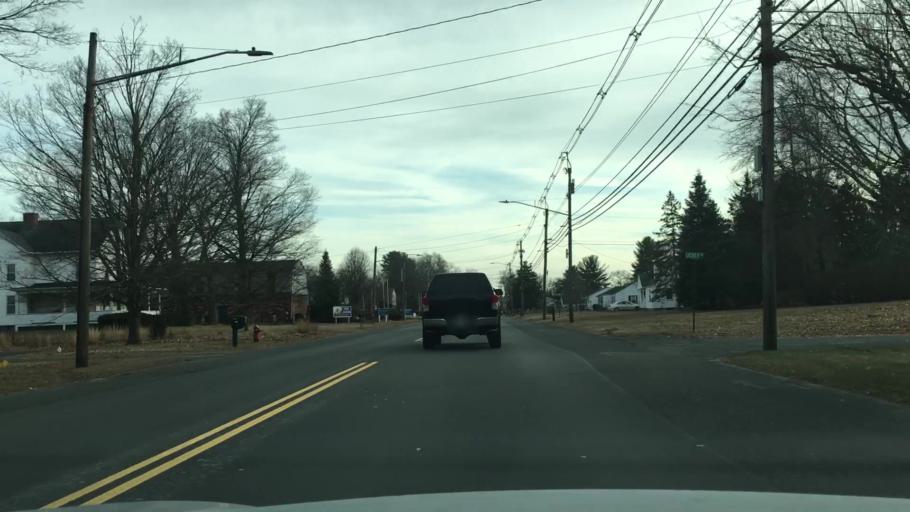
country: US
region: Massachusetts
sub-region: Hampden County
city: Westfield
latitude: 42.1016
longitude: -72.7640
